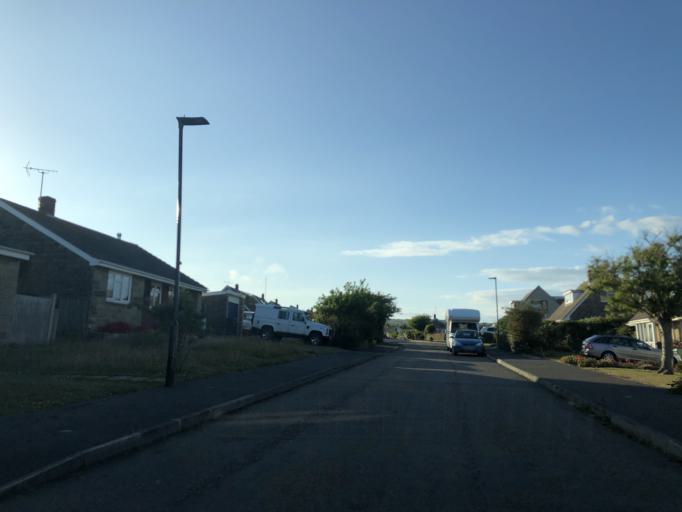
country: GB
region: England
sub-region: Isle of Wight
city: Shalfleet
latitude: 50.6413
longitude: -1.4010
